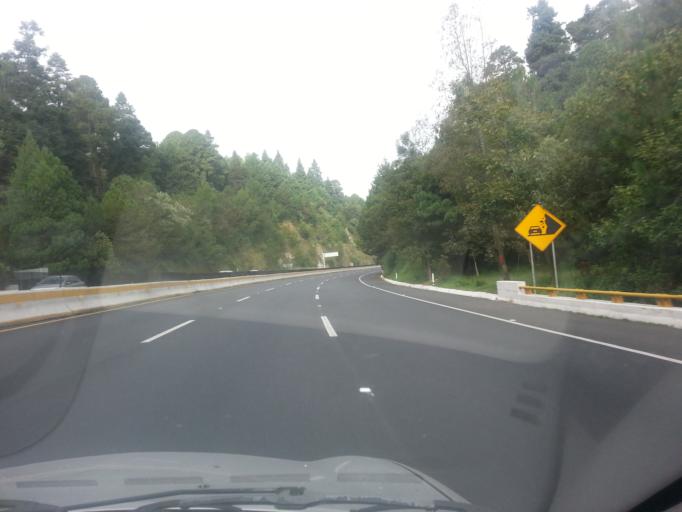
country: MX
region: Mexico City
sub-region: Cuajimalpa de Morelos
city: San Lorenzo Acopilco
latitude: 19.3346
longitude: -99.3037
